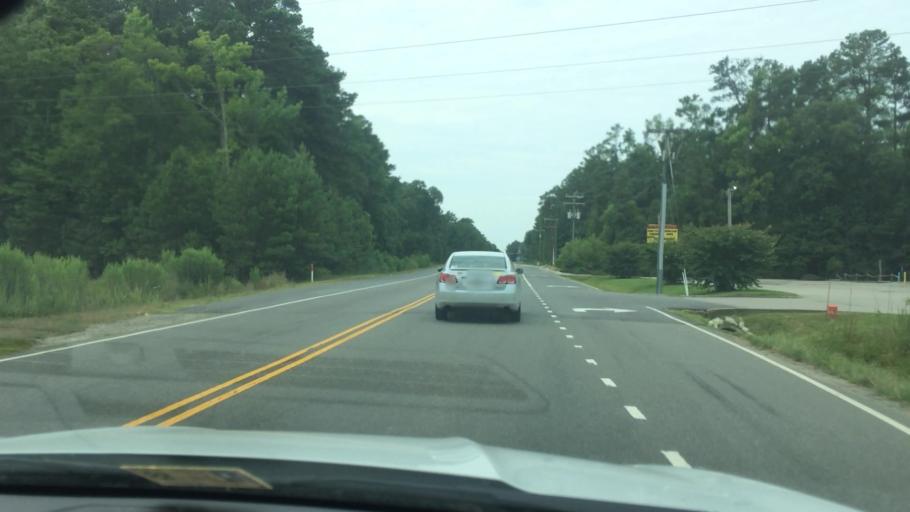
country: US
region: Virginia
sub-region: York County
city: Yorktown
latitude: 37.1569
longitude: -76.5036
